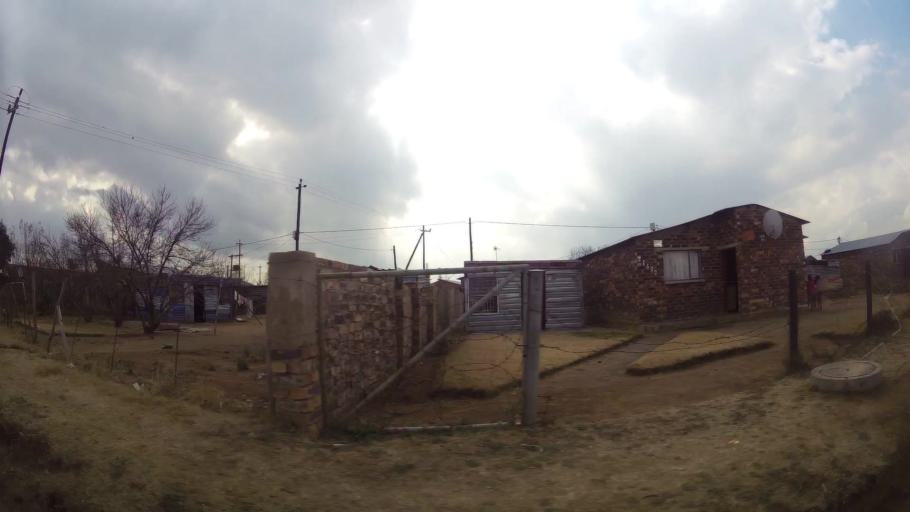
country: ZA
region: Orange Free State
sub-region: Fezile Dabi District Municipality
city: Sasolburg
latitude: -26.8626
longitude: 27.9009
